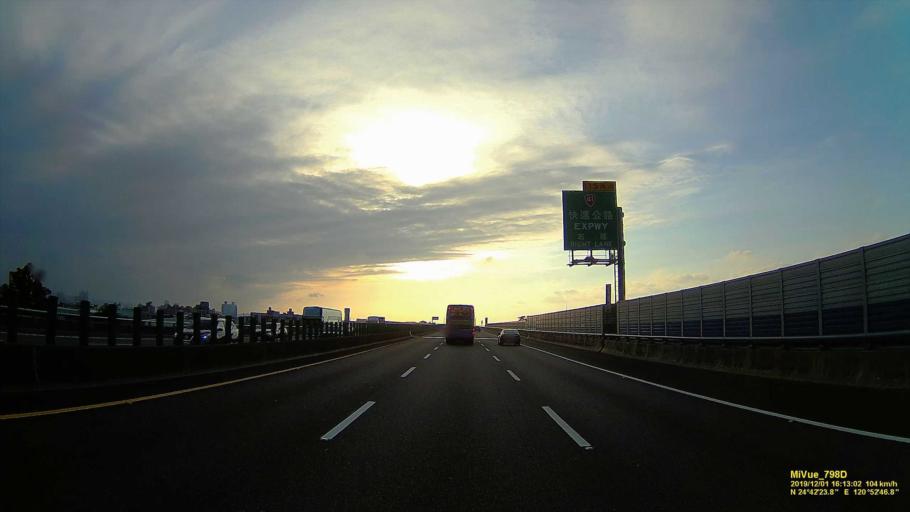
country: TW
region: Taiwan
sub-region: Hsinchu
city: Hsinchu
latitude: 24.7069
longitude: 120.8799
